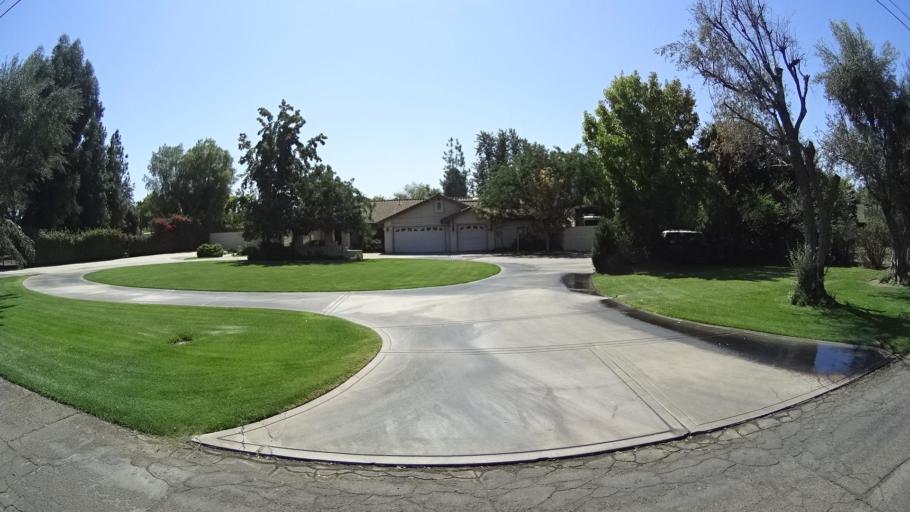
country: US
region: California
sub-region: San Diego County
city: Granite Hills
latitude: 32.8041
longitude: -116.9162
